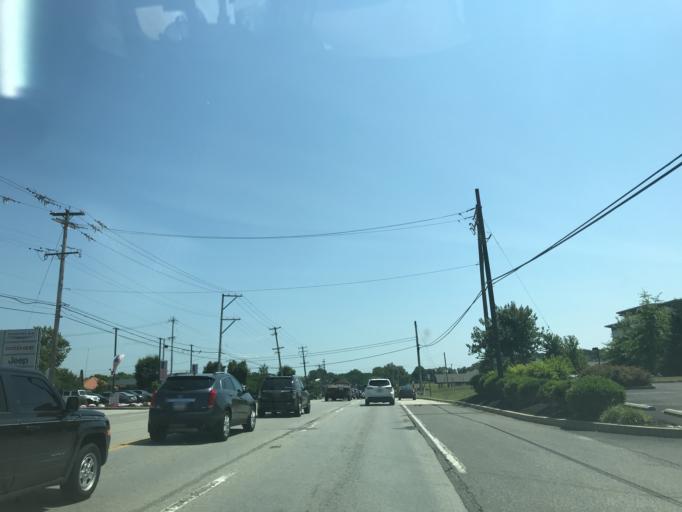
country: US
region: Pennsylvania
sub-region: Delaware County
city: Chester Heights
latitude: 39.8686
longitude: -75.5445
